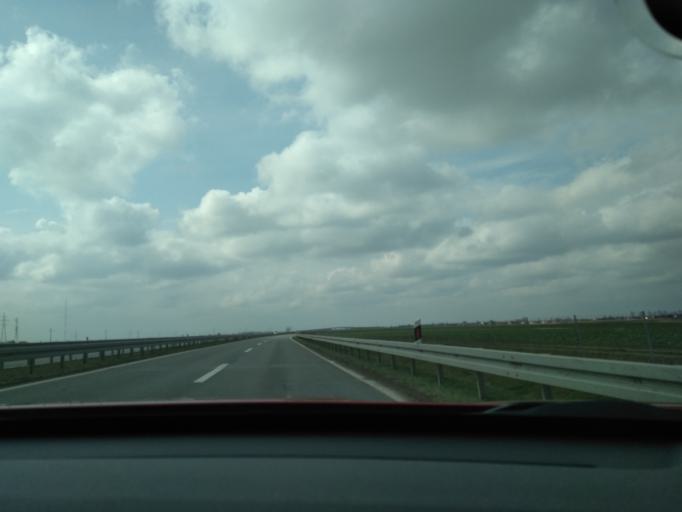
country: HR
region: Osjecko-Baranjska
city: Visnjevac
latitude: 45.5580
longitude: 18.6075
